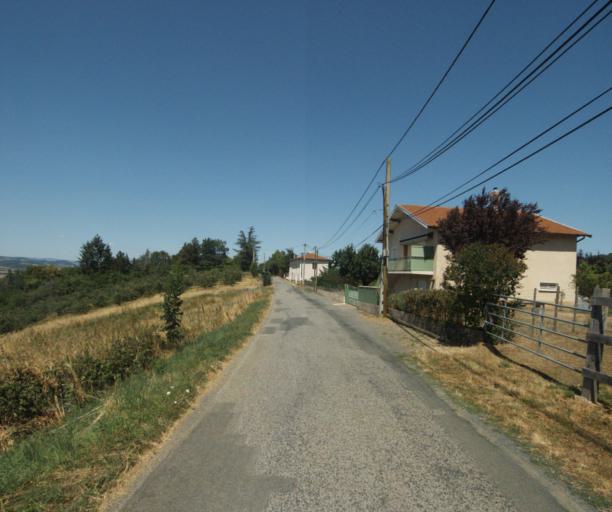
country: FR
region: Rhone-Alpes
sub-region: Departement du Rhone
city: Courzieu
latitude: 45.7536
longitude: 4.5850
